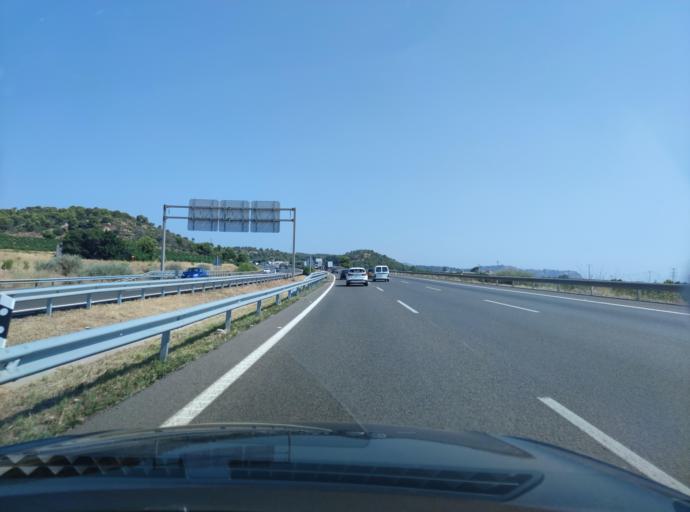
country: ES
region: Valencia
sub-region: Provincia de Valencia
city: Pucol
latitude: 39.6431
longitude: -0.3003
